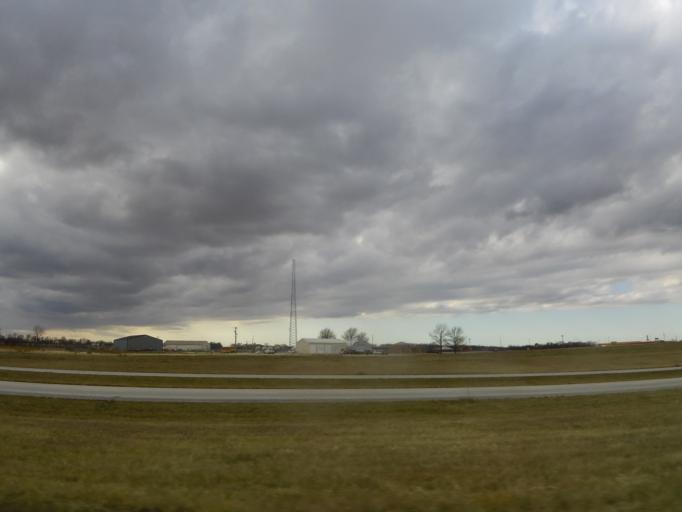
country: US
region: Missouri
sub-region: Ralls County
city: New London
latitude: 39.5730
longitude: -91.3991
